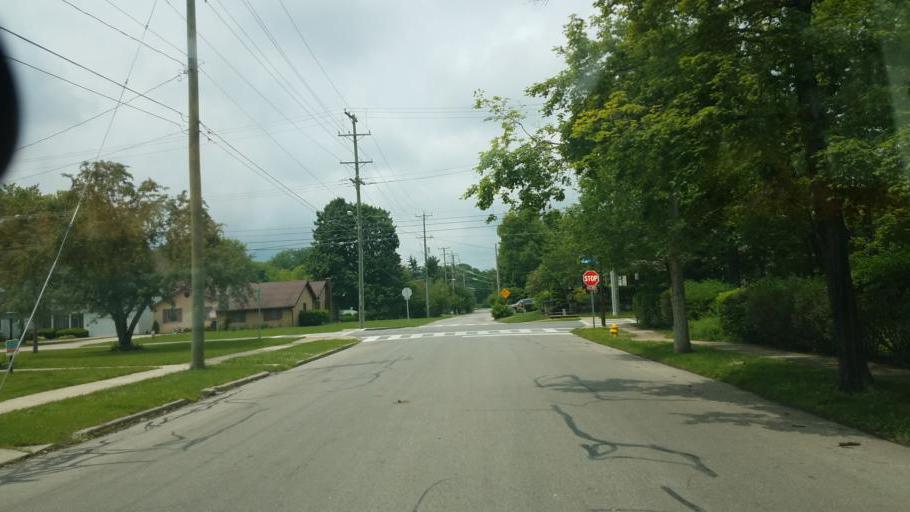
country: US
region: Ohio
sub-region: Delaware County
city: Delaware
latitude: 40.3061
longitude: -83.0780
